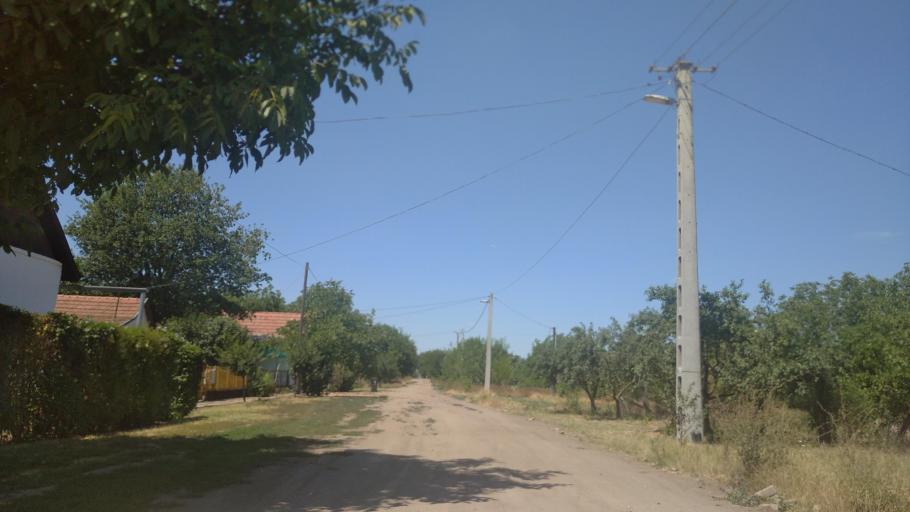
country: HU
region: Bekes
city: Oroshaza
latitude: 46.5594
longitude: 20.6188
